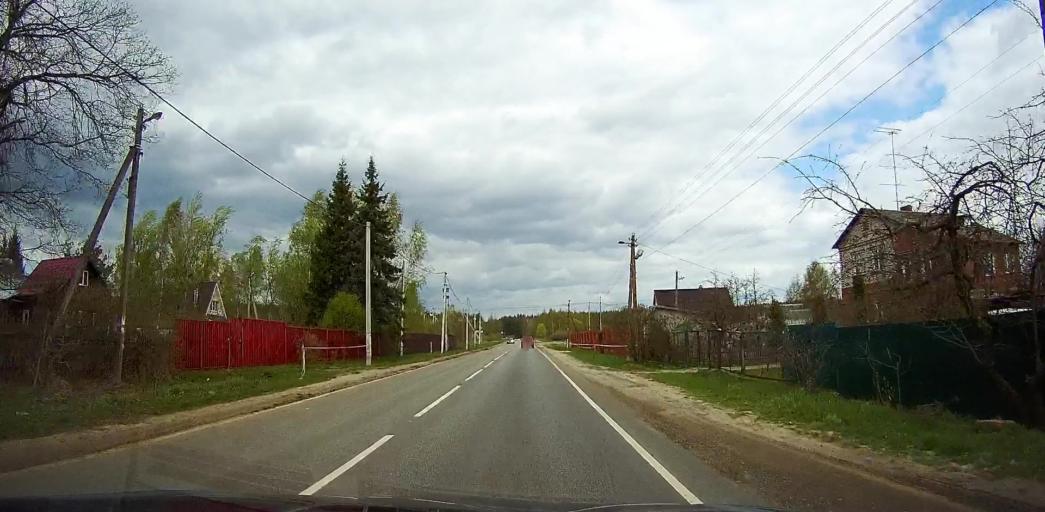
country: RU
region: Moskovskaya
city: Ashitkovo
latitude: 55.4652
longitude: 38.6067
